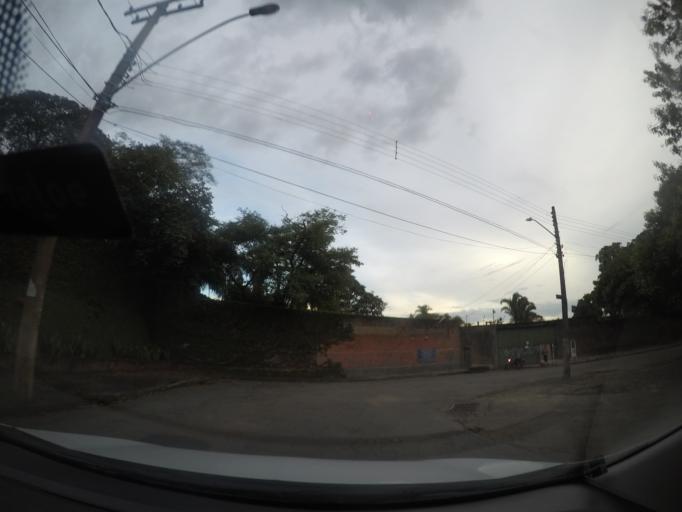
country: BR
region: Goias
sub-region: Goiania
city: Goiania
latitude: -16.6519
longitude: -49.2236
